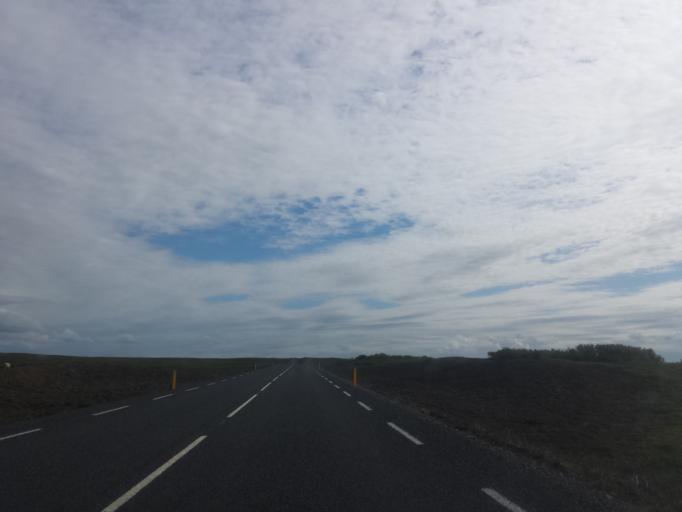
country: IS
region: Northeast
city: Husavik
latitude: 65.9941
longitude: -16.5657
